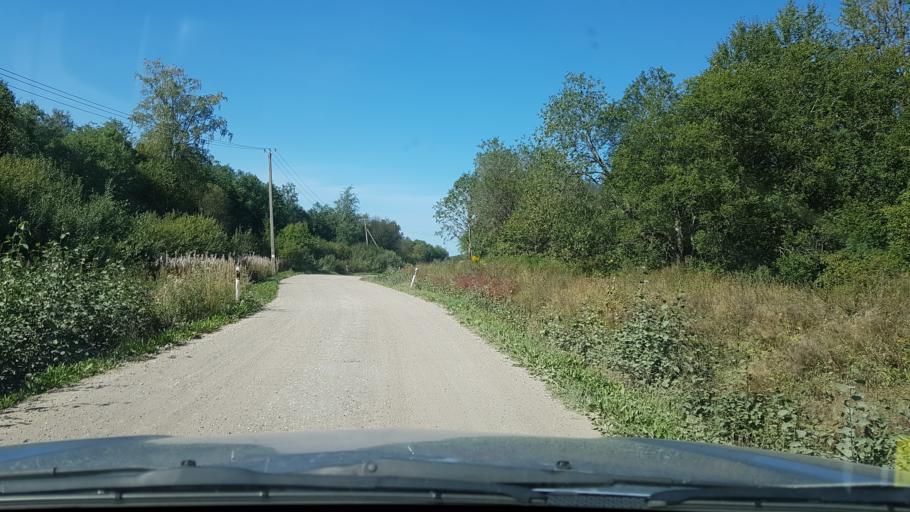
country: EE
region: Ida-Virumaa
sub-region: Sillamaee linn
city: Sillamae
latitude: 59.3767
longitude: 27.7767
